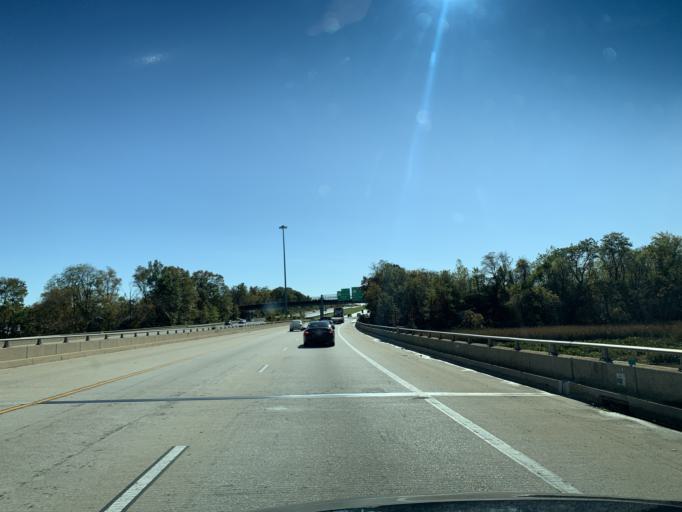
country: US
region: Maryland
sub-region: Baltimore County
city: Rosedale
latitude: 39.3038
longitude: -76.5010
